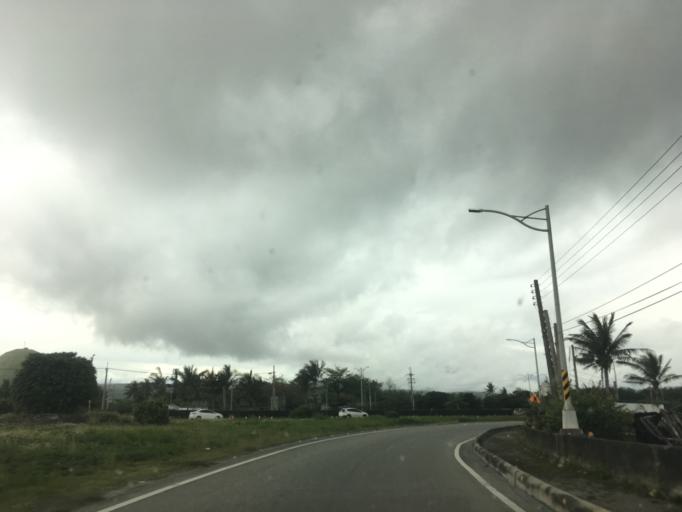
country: TW
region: Taiwan
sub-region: Taitung
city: Taitung
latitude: 22.7760
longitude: 121.1748
